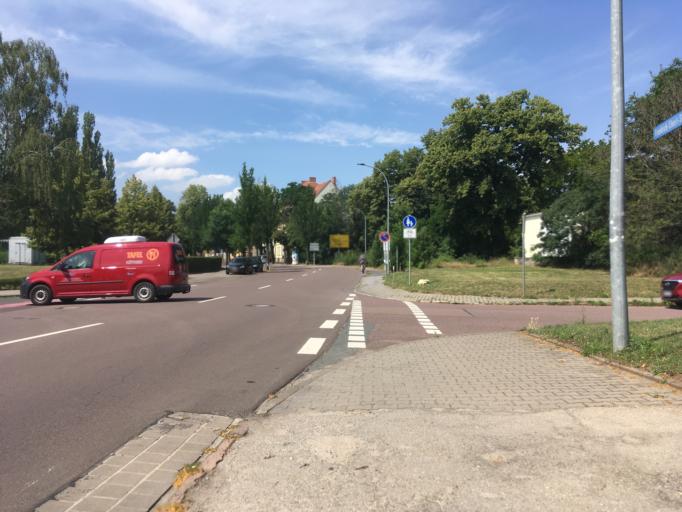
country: DE
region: Saxony-Anhalt
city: Koethen
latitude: 51.7545
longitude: 11.9933
